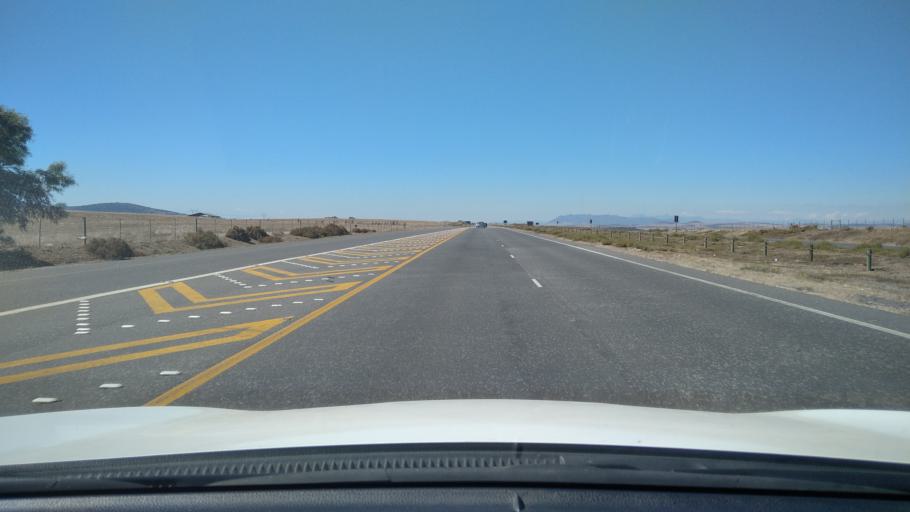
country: ZA
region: Western Cape
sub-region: City of Cape Town
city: Atlantis
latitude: -33.6591
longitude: 18.5615
